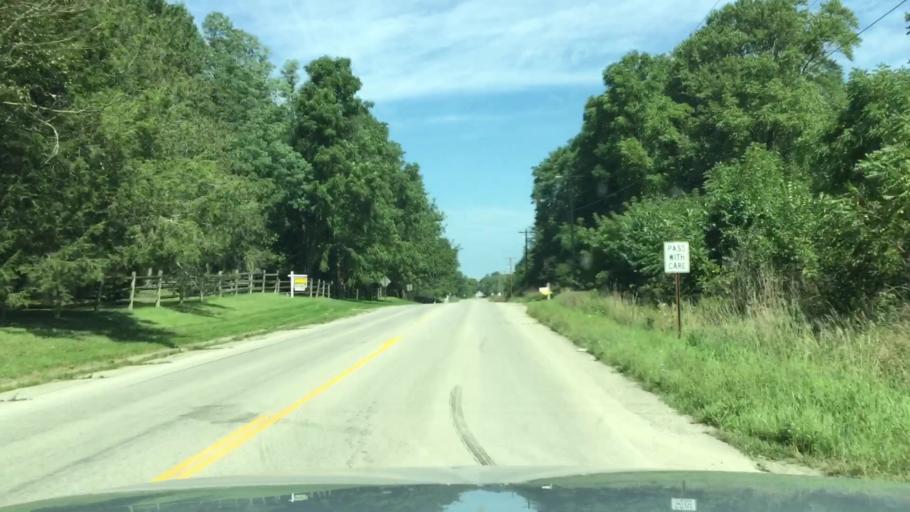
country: US
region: Michigan
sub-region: Lenawee County
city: Manitou Beach-Devils Lake
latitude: 42.0304
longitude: -84.2763
